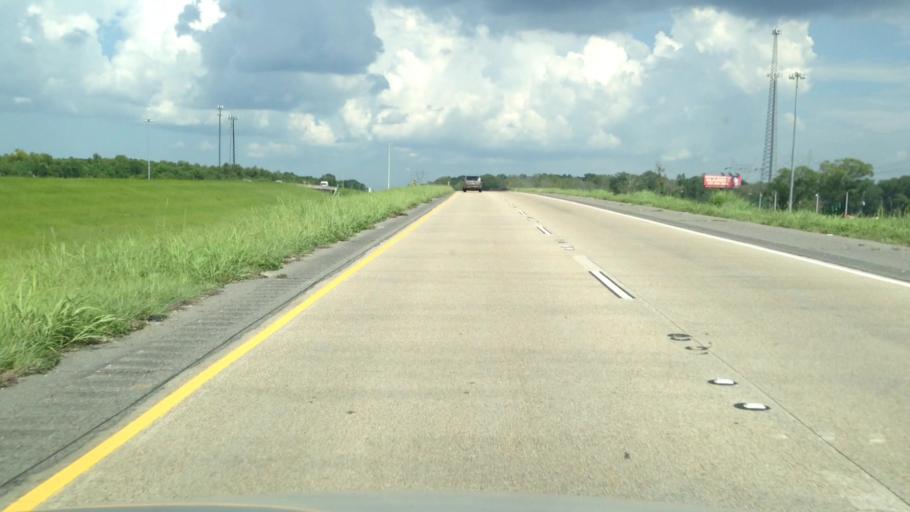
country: US
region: Louisiana
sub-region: Ascension Parish
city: Sorrento
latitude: 30.1725
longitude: -90.8793
